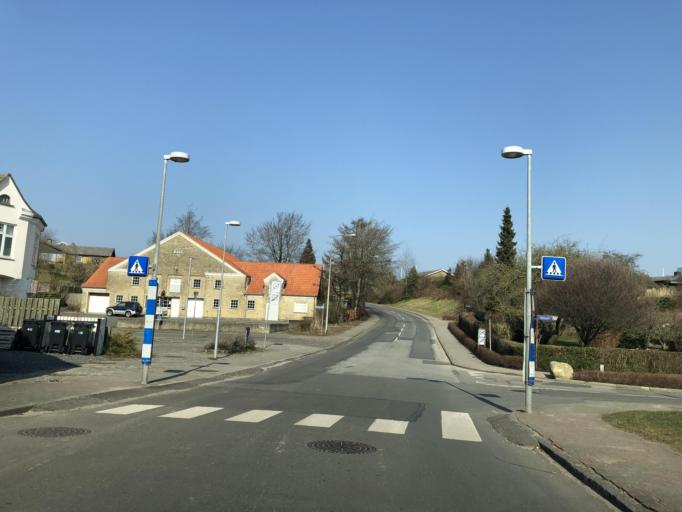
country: DK
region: South Denmark
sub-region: Sonderborg Kommune
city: Nordborg
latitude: 55.0588
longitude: 9.7418
